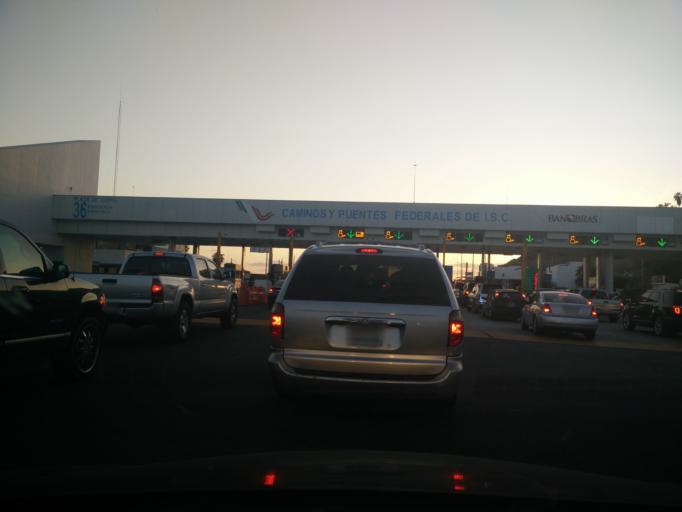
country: MX
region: Baja California
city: El Sauzal
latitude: 31.9033
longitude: -116.7321
